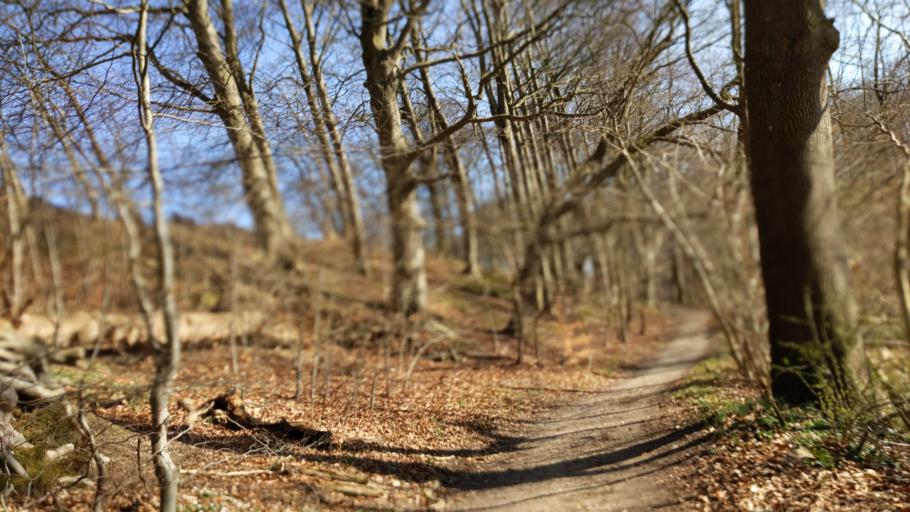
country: DE
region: Schleswig-Holstein
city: Timmendorfer Strand
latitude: 53.9850
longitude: 10.8241
